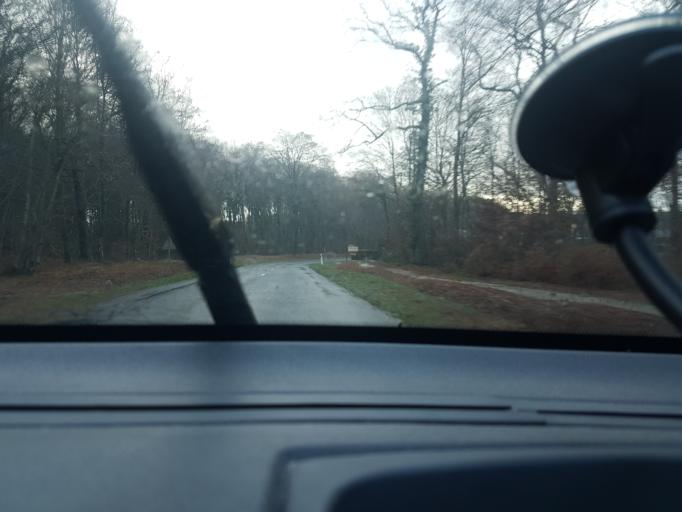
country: FR
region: Franche-Comte
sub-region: Territoire de Belfort
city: Danjoutin
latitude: 47.6089
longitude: 6.8503
